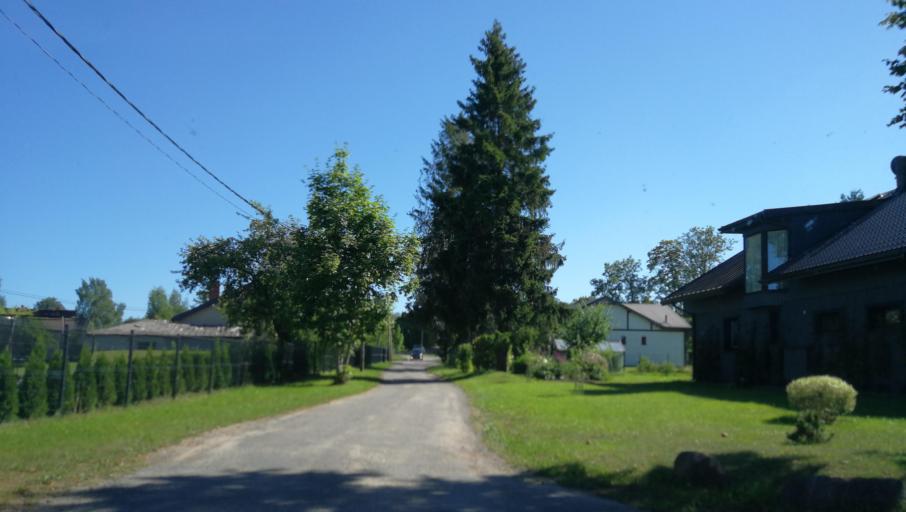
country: LV
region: Cesu Rajons
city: Cesis
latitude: 57.3040
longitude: 25.2485
